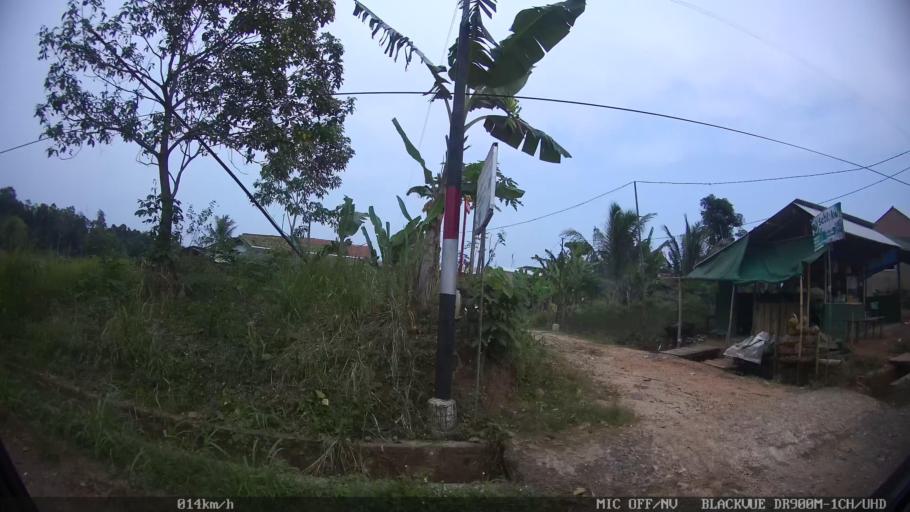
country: ID
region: Lampung
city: Panjang
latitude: -5.4203
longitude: 105.3565
